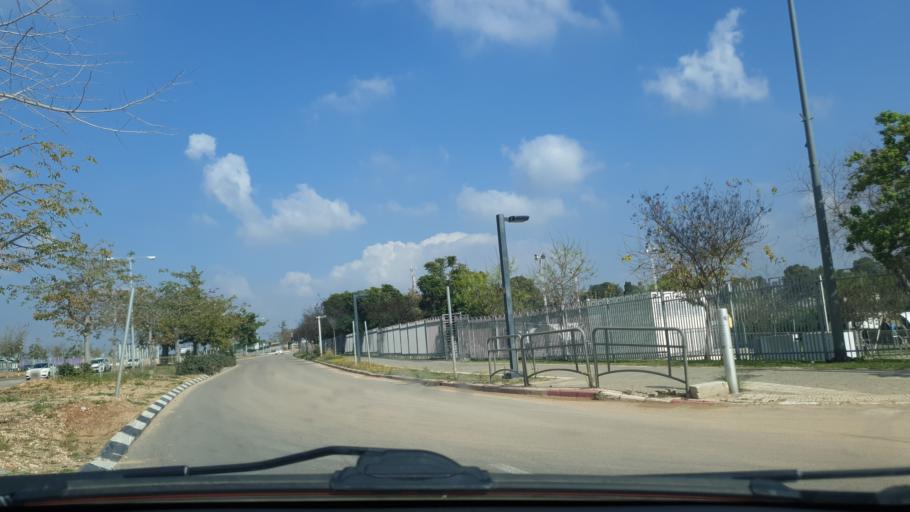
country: IL
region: Central District
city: Bet Dagan
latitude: 31.9666
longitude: 34.8252
